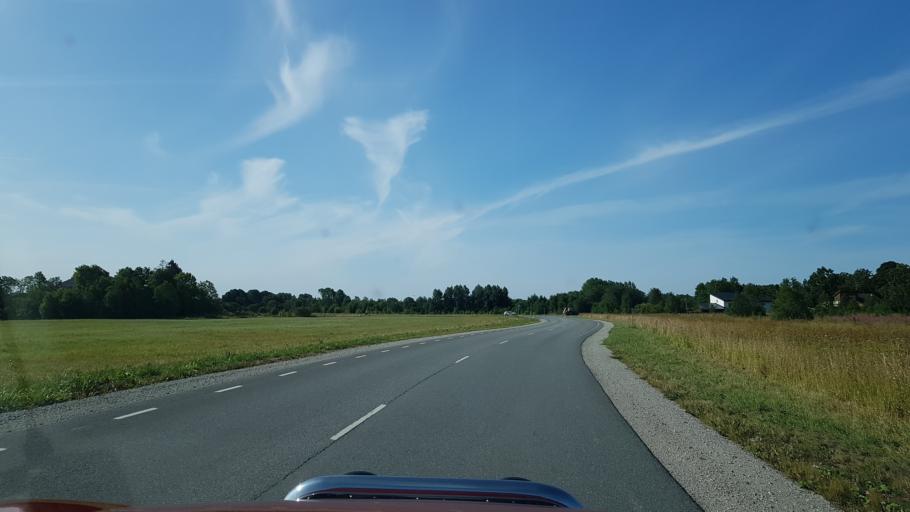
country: EE
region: Harju
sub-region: Rae vald
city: Jueri
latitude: 59.3747
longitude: 24.9257
